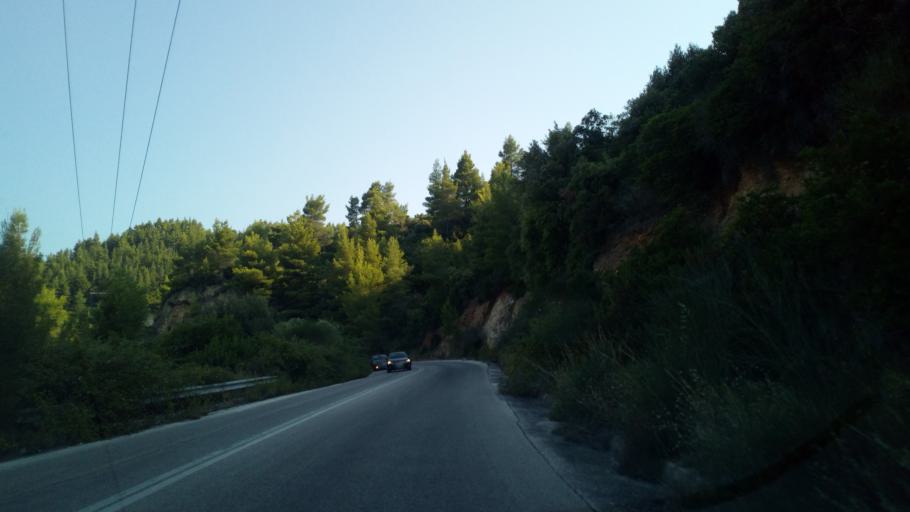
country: GR
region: Central Macedonia
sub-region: Nomos Chalkidikis
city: Neos Marmaras
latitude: 40.1660
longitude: 23.8652
